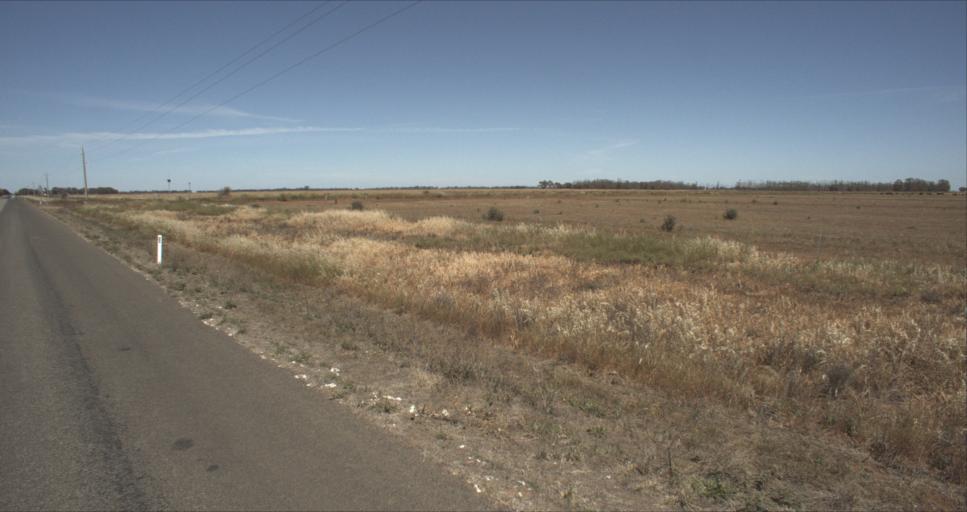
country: AU
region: New South Wales
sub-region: Leeton
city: Leeton
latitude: -34.4811
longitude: 146.2905
